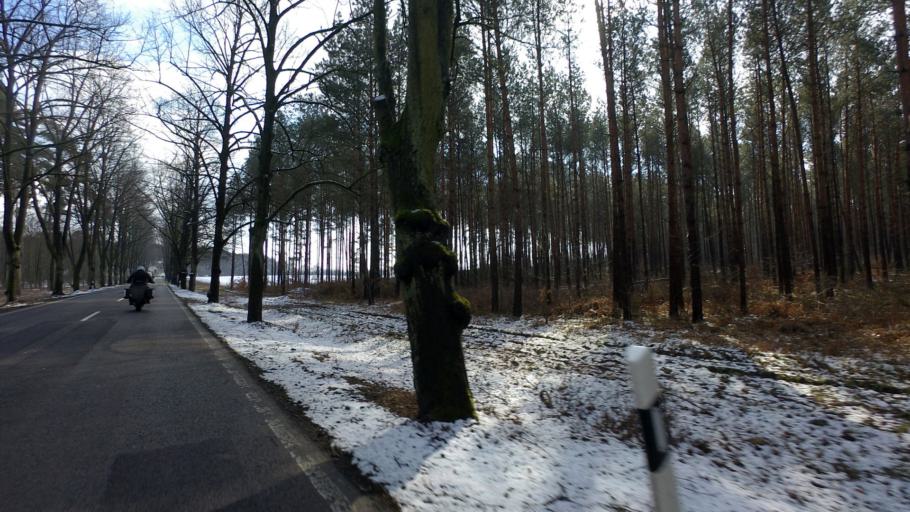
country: DE
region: Brandenburg
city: Rudnitz
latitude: 52.7023
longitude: 13.6428
